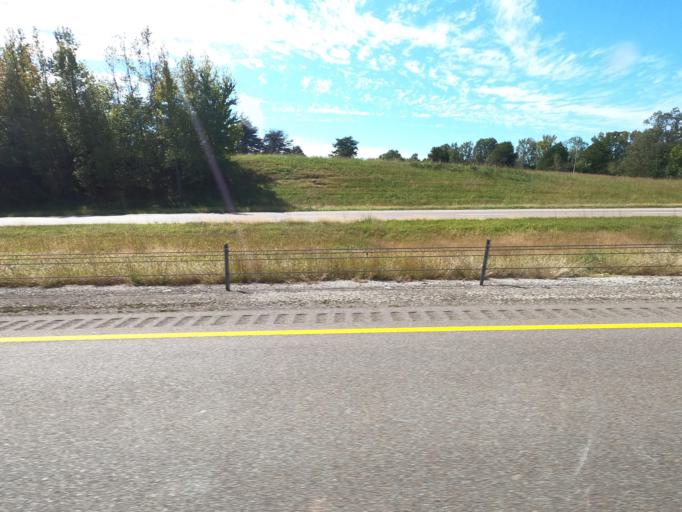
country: US
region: Tennessee
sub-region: Crockett County
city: Bells
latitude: 35.6744
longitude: -88.9619
